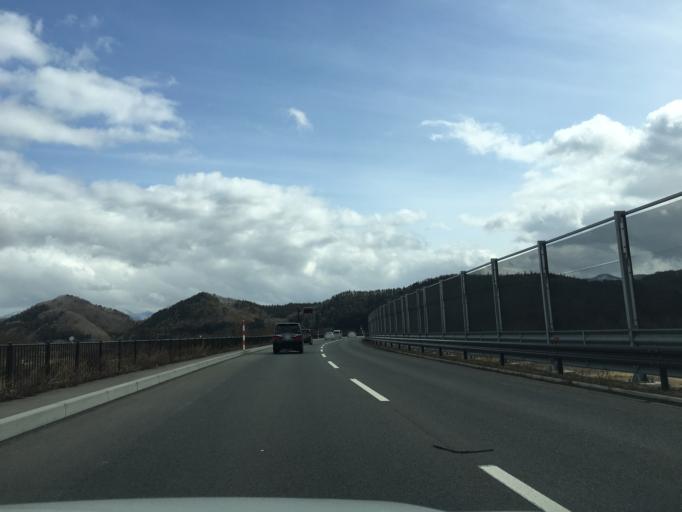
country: JP
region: Akita
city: Hanawa
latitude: 40.2275
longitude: 140.7129
